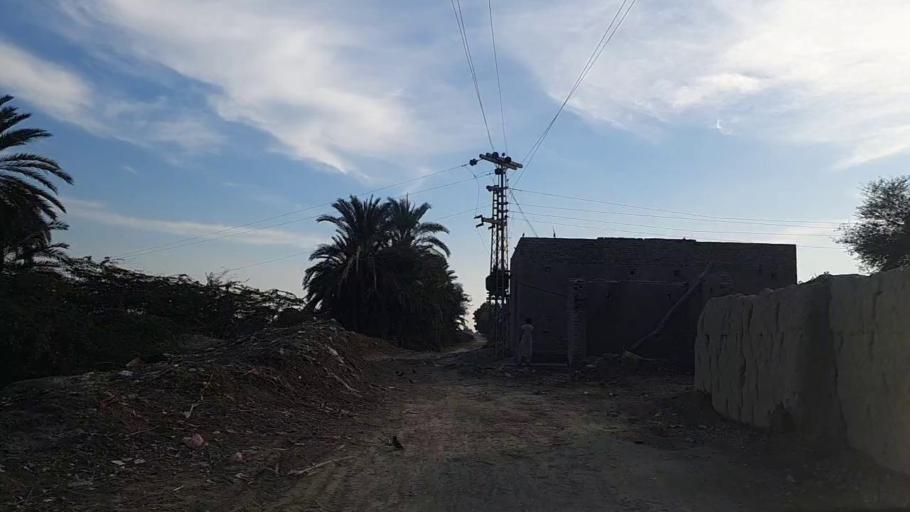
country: PK
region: Sindh
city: Bandhi
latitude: 26.5617
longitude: 68.2786
